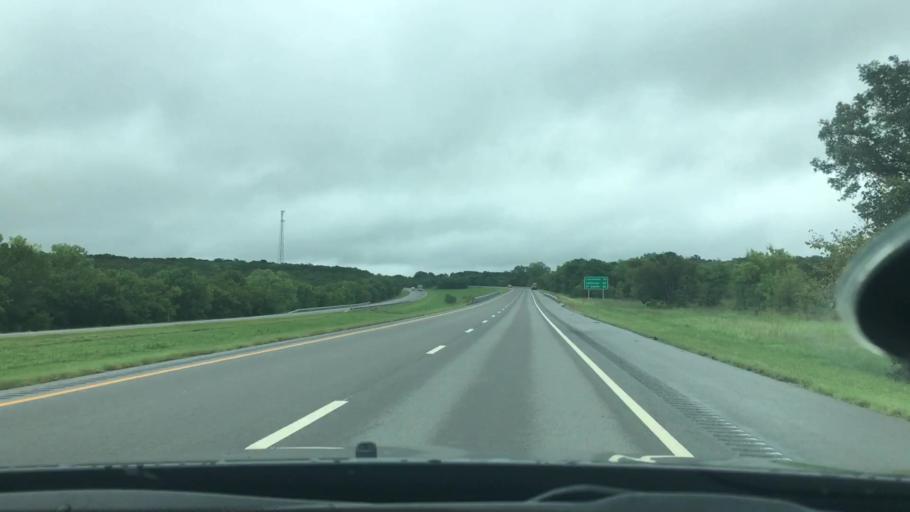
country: US
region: Oklahoma
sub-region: Okmulgee County
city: Henryetta
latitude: 35.4347
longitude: -95.8181
